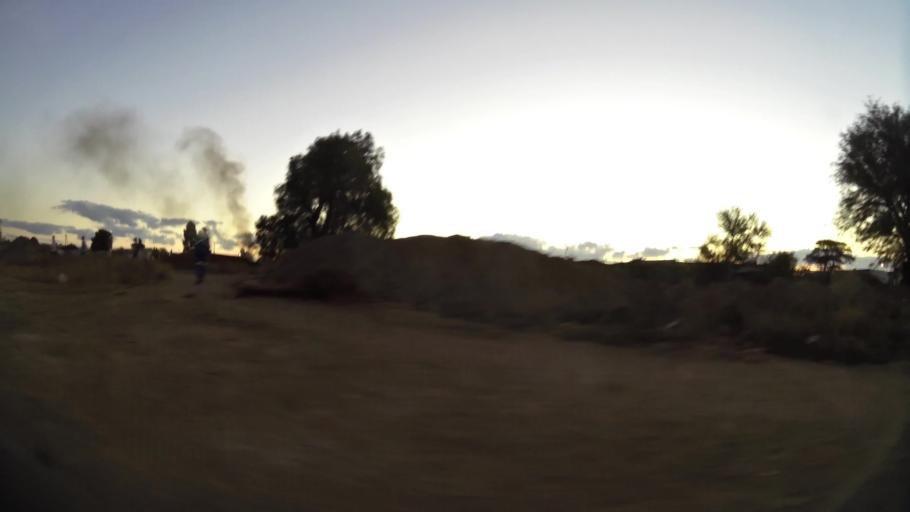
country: ZA
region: Northern Cape
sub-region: Frances Baard District Municipality
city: Kimberley
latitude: -28.7217
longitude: 24.7624
